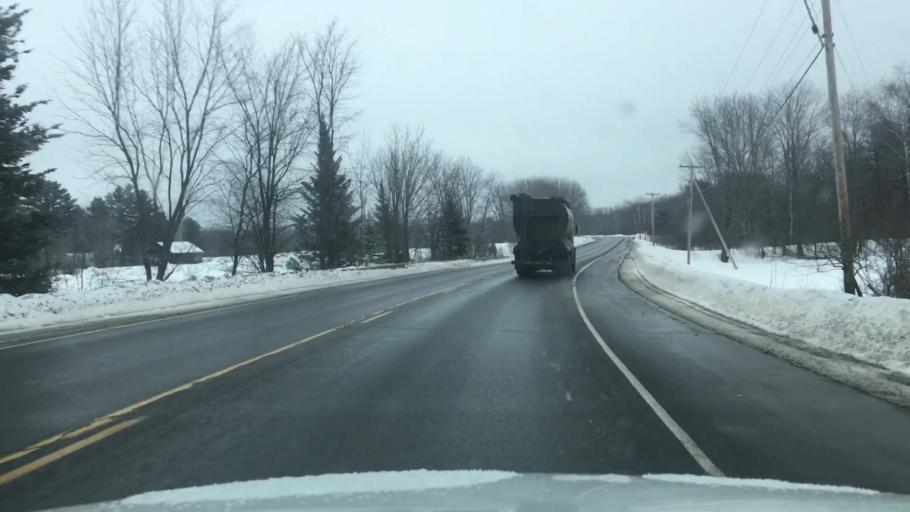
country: US
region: Maine
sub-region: Franklin County
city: New Sharon
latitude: 44.6370
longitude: -70.0492
